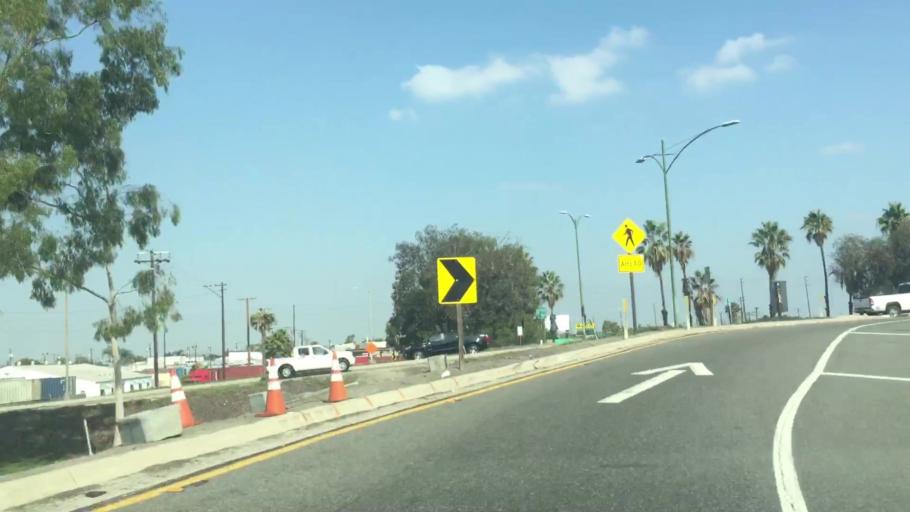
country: US
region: California
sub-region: Los Angeles County
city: Long Beach
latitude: 33.7822
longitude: -118.2086
